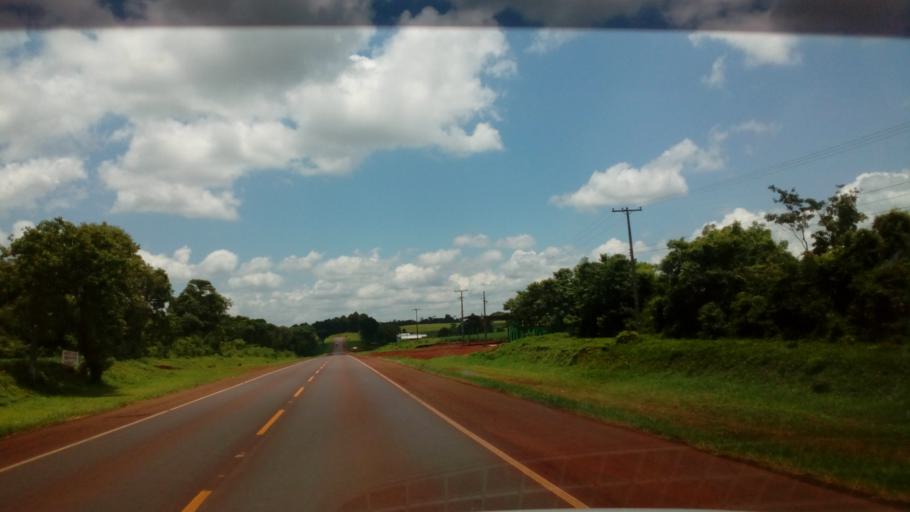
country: PY
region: Itapua
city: Arquitecto Tomas Romero Pereira
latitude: -26.4484
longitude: -55.2538
